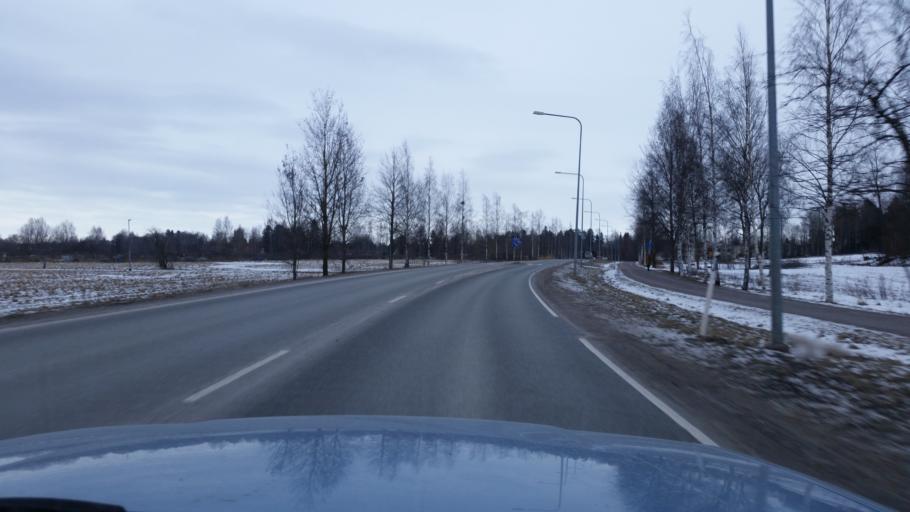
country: FI
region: Uusimaa
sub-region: Helsinki
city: Vantaa
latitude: 60.2481
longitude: 24.9771
